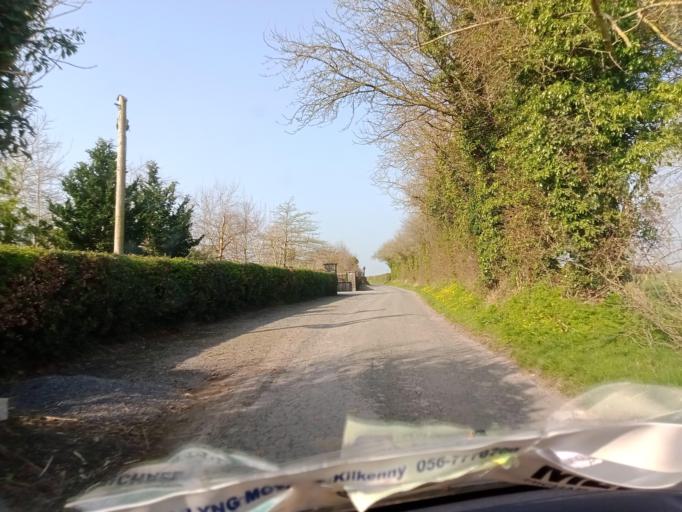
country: IE
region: Leinster
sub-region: Kilkenny
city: Callan
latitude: 52.5206
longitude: -7.4033
